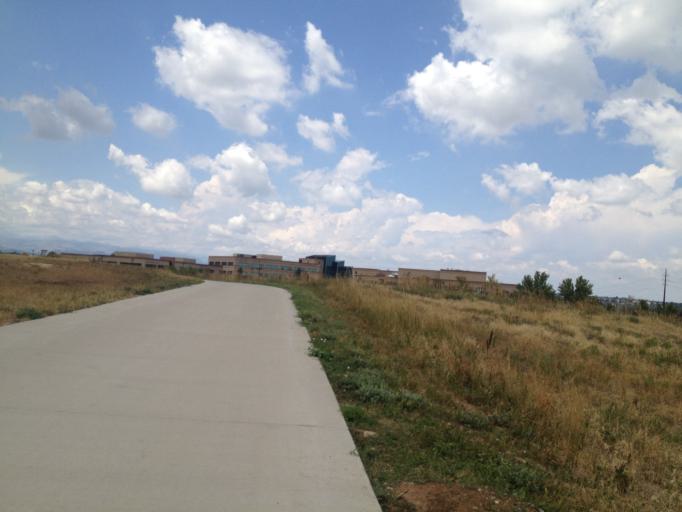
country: US
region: Colorado
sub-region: Boulder County
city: Superior
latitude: 39.9495
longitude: -105.1503
